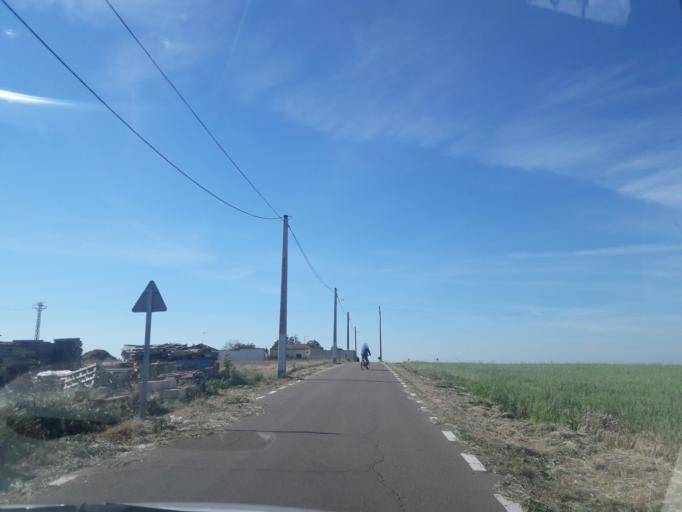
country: ES
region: Castille and Leon
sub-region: Provincia de Salamanca
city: Parada de Rubiales
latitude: 41.1454
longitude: -5.4381
